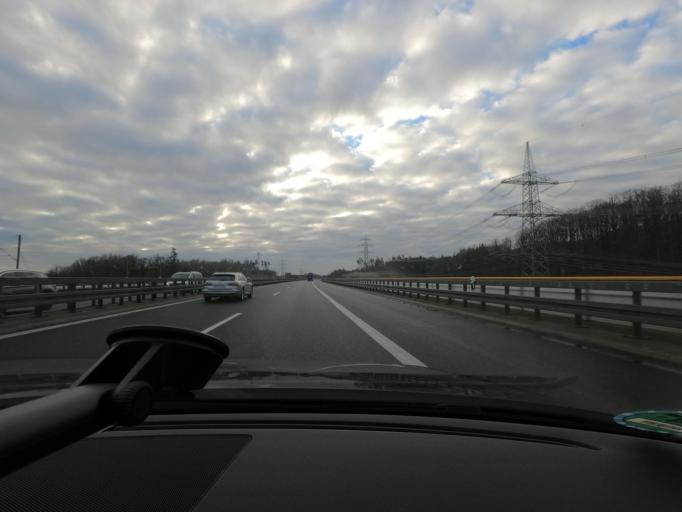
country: DE
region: Bavaria
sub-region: Upper Franconia
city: Rodental
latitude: 50.2787
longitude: 11.0146
